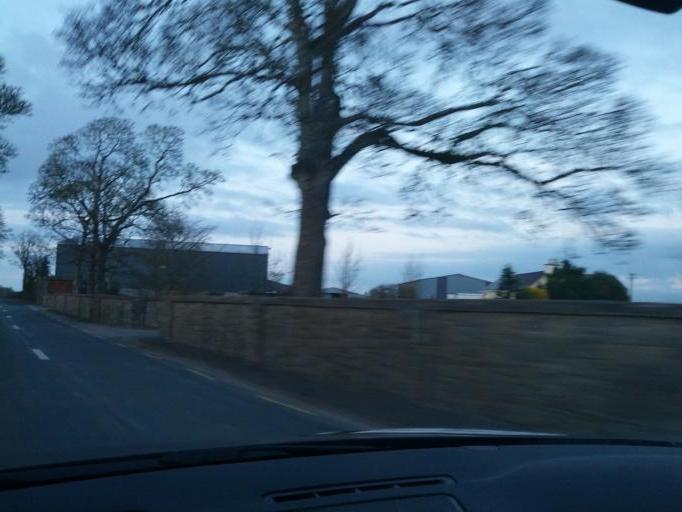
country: IE
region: Connaught
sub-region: County Galway
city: Portumna
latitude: 53.0341
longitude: -8.1174
